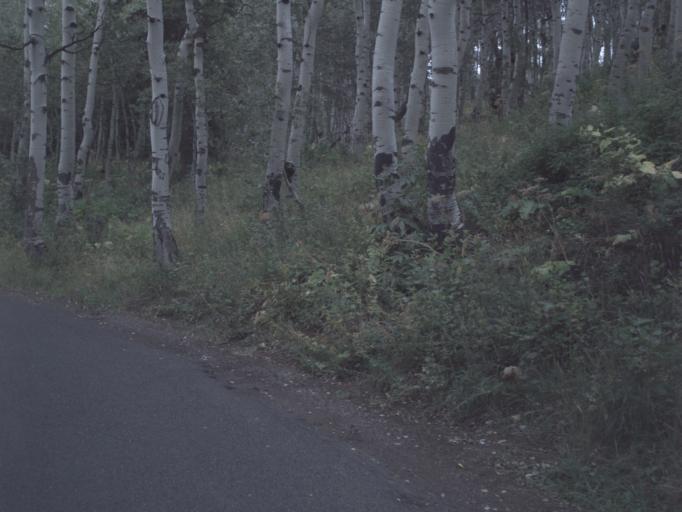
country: US
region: Utah
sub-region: Utah County
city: Lindon
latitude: 40.4242
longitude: -111.6062
